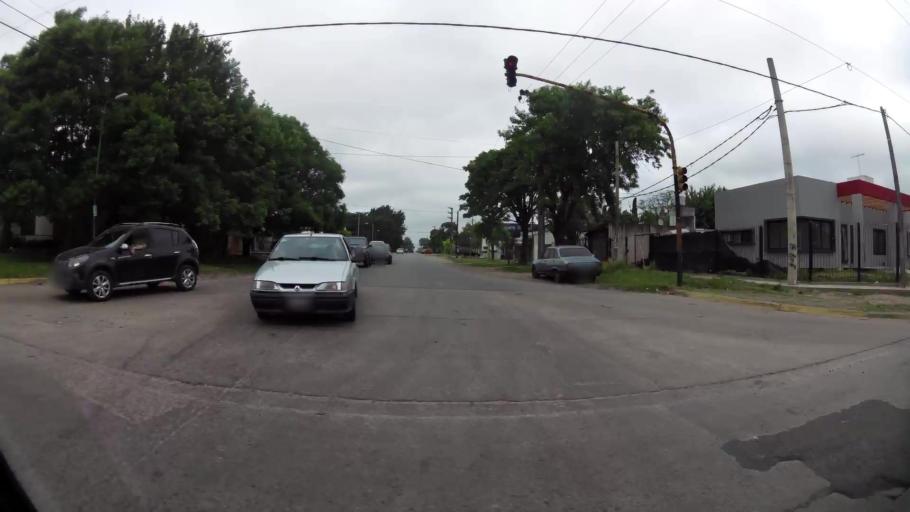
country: AR
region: Buenos Aires
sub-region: Partido de La Plata
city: La Plata
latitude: -34.9505
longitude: -57.9989
